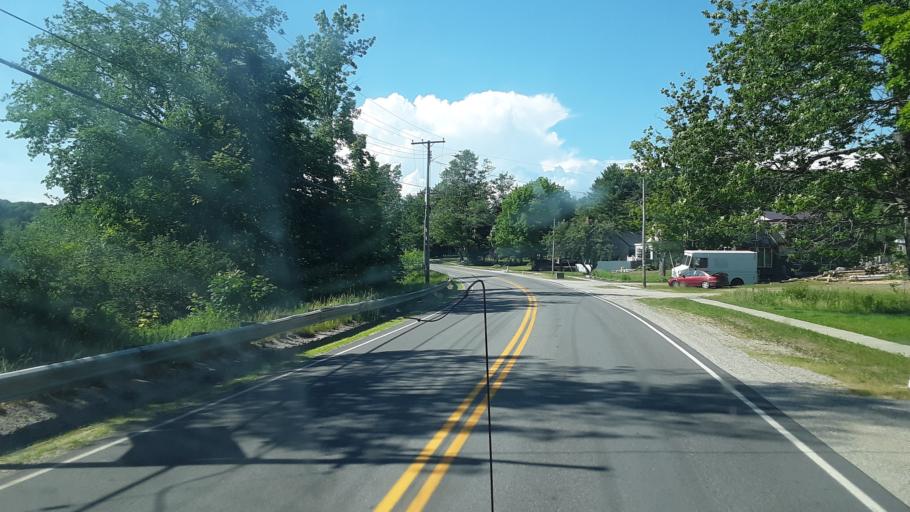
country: US
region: Maine
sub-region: Washington County
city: Cherryfield
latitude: 44.6035
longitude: -67.9250
